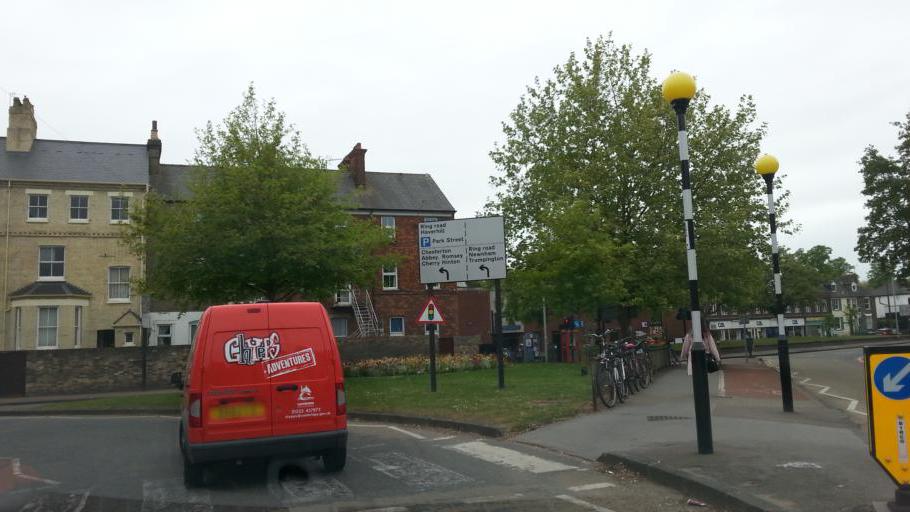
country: GB
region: England
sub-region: Cambridgeshire
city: Cambridge
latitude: 52.2149
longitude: 0.1253
